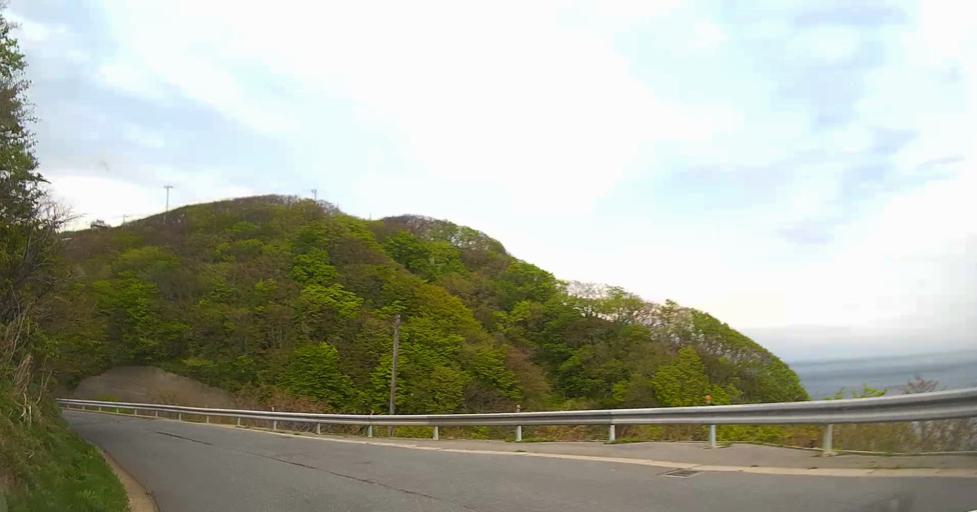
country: JP
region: Aomori
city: Shimokizukuri
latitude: 41.2553
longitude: 140.3512
